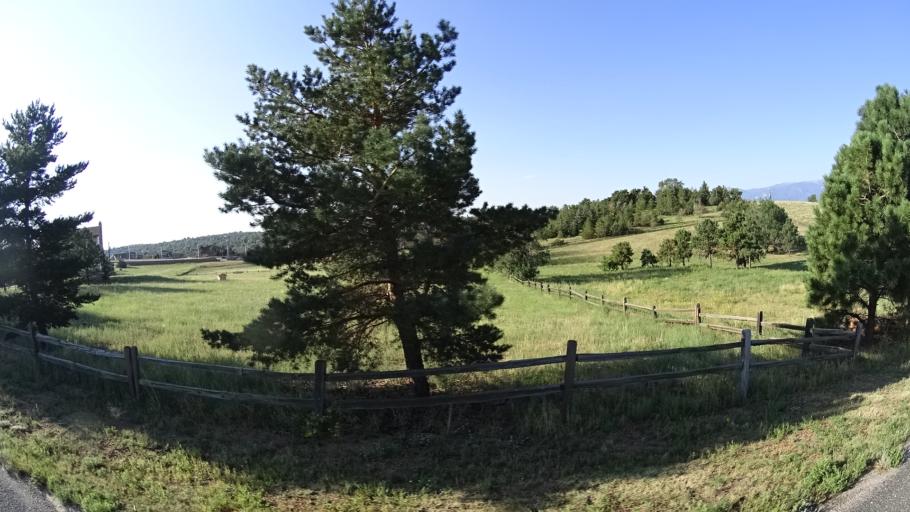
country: US
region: Colorado
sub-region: El Paso County
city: Black Forest
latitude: 38.9367
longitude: -104.7699
